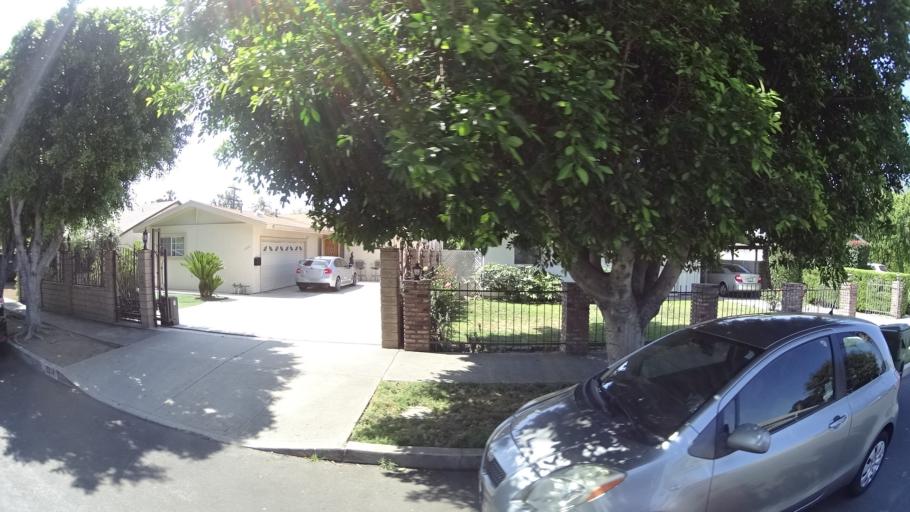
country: US
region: California
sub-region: Los Angeles County
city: Van Nuys
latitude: 34.2039
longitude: -118.4647
